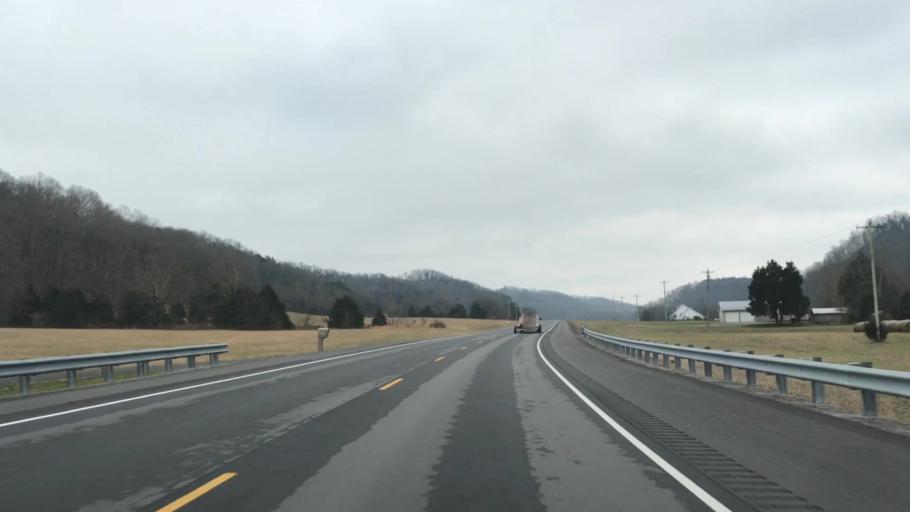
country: US
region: Kentucky
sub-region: Cumberland County
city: Burkesville
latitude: 36.8457
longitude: -85.3715
